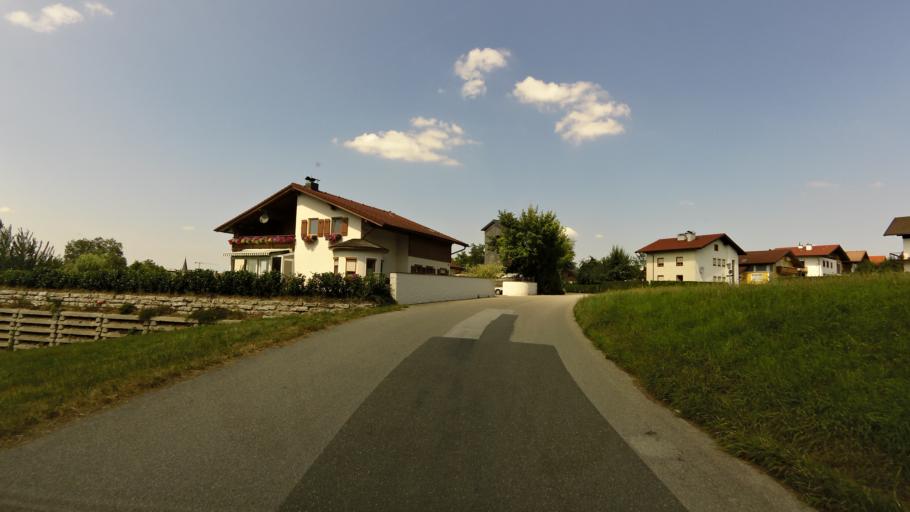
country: AT
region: Salzburg
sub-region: Politischer Bezirk Salzburg-Umgebung
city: Henndorf am Wallersee
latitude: 47.8955
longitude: 13.1907
